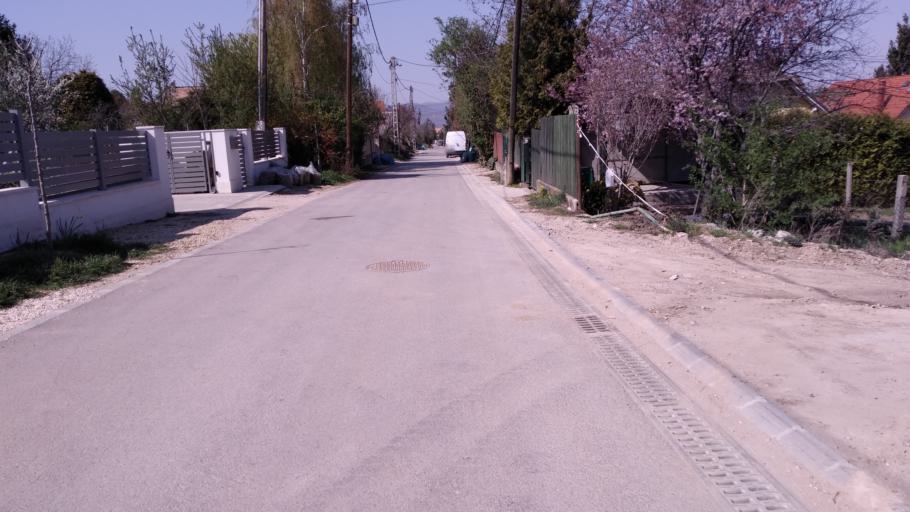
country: HU
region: Pest
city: Budakalasz
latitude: 47.6107
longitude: 19.0529
